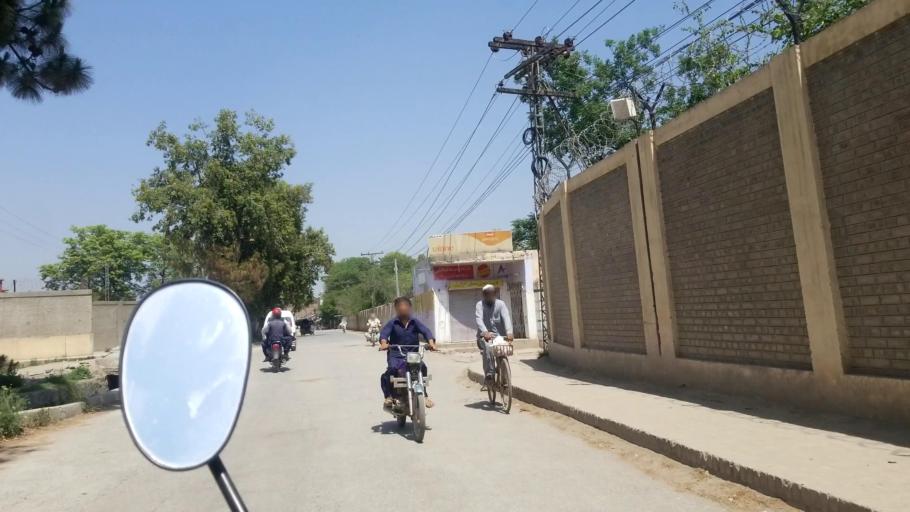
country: PK
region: Khyber Pakhtunkhwa
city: Peshawar
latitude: 34.0202
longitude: 71.4841
